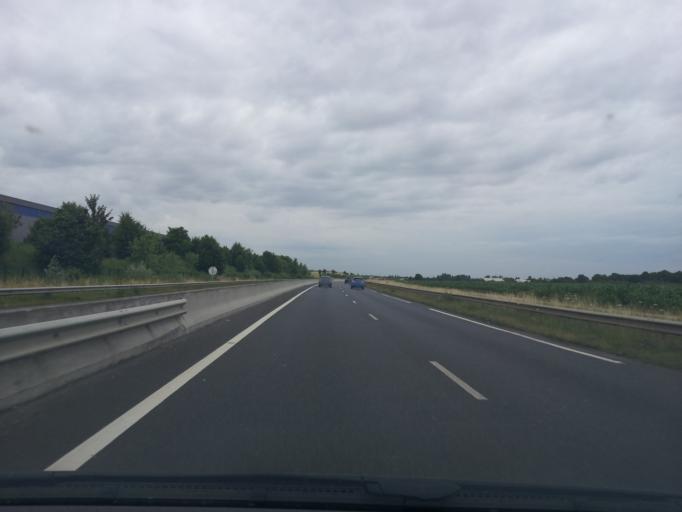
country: FR
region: Ile-de-France
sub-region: Departement de l'Essonne
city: Bretigny-sur-Orge
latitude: 48.5894
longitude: 2.3081
